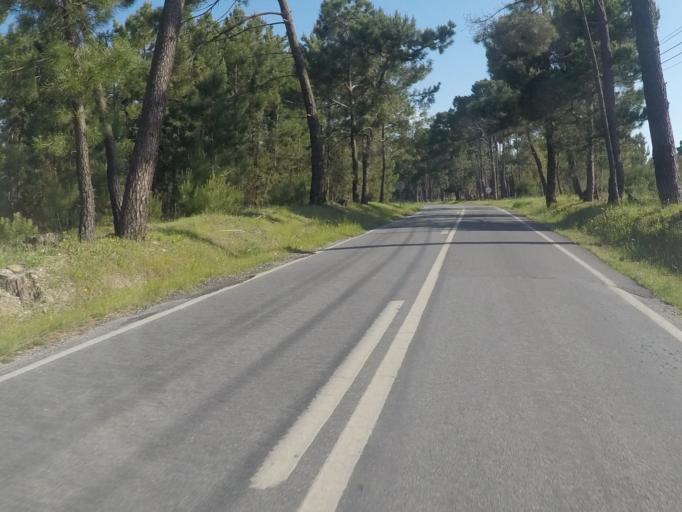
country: PT
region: Setubal
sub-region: Sesimbra
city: Sesimbra
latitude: 38.4879
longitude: -9.1578
